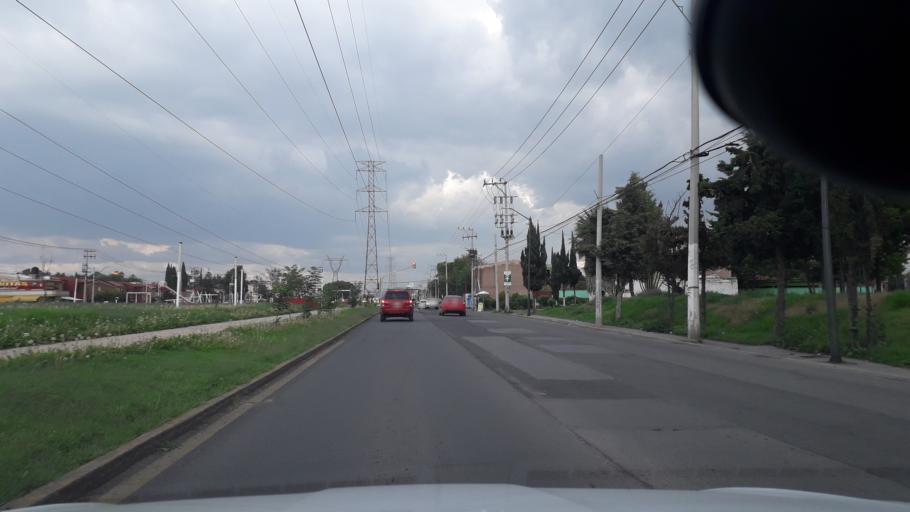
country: MX
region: Mexico
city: Santiago Teyahualco
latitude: 19.6412
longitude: -99.1235
